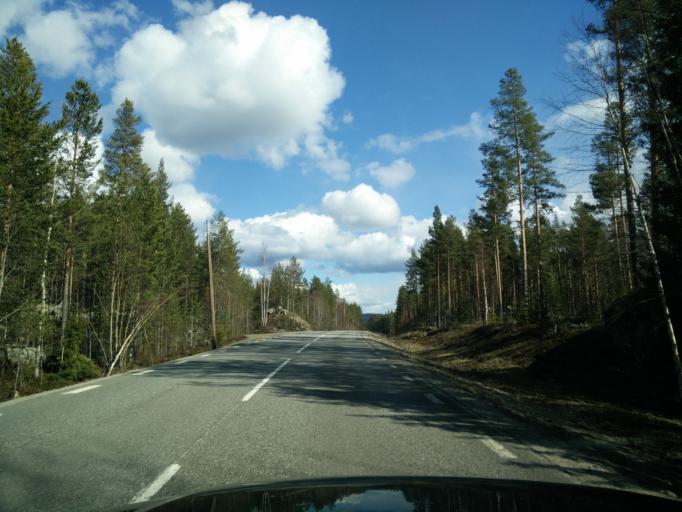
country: SE
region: Jaemtland
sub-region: Braecke Kommun
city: Braecke
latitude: 62.4510
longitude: 14.9428
